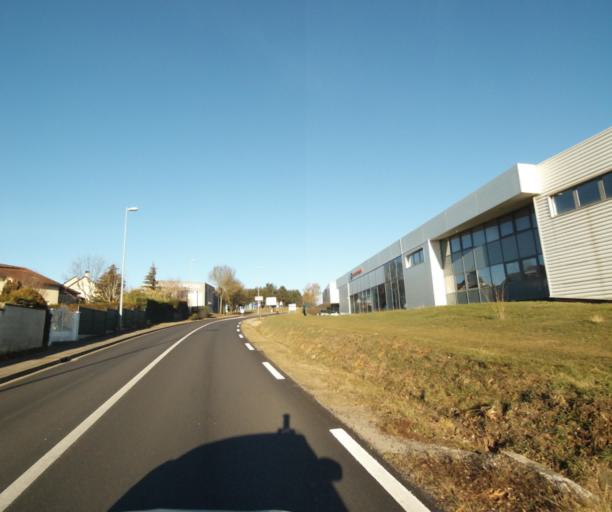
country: FR
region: Lorraine
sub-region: Departement de Meurthe-et-Moselle
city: Laxou
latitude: 48.6896
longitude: 6.1307
